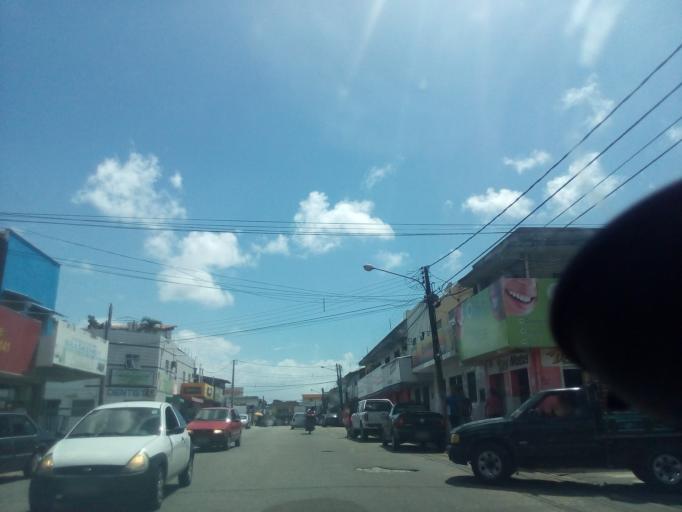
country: BR
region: Rio Grande do Norte
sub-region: Natal
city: Natal
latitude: -5.8254
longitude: -35.2375
